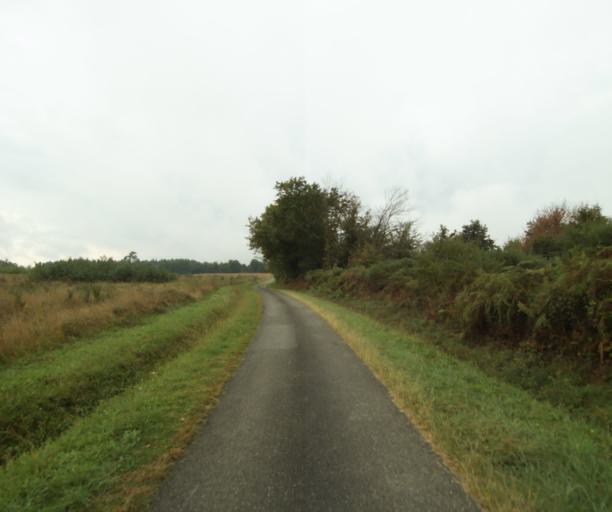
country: FR
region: Midi-Pyrenees
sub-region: Departement du Gers
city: Cazaubon
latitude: 43.9246
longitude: -0.1455
